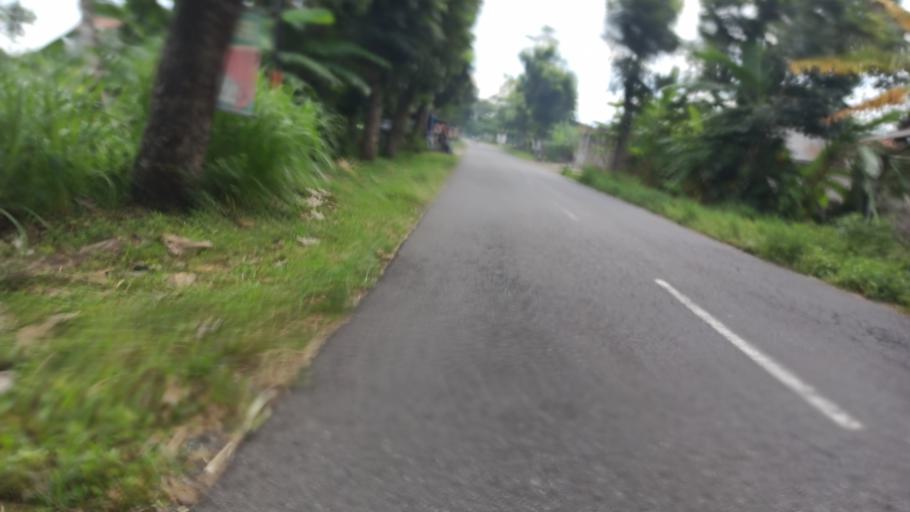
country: ID
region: Daerah Istimewa Yogyakarta
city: Sleman
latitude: -7.6973
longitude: 110.2914
